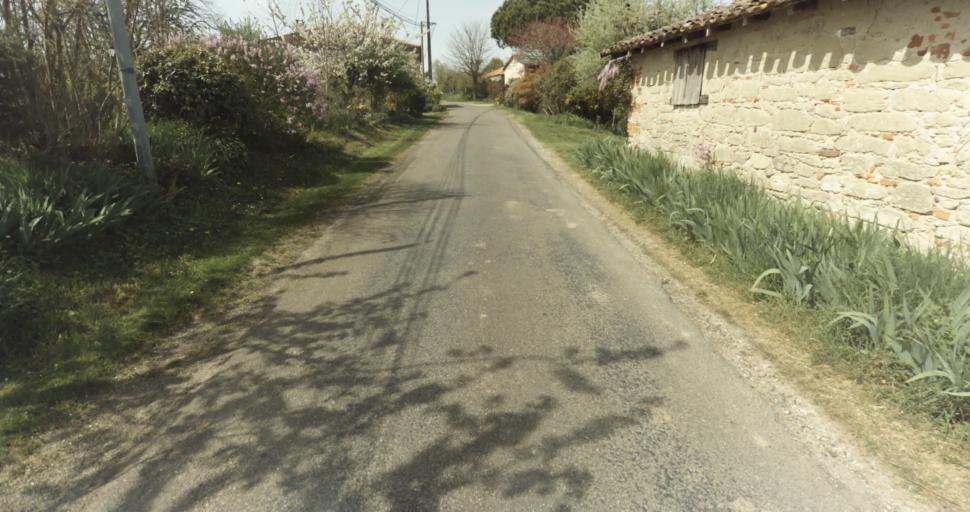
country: FR
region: Midi-Pyrenees
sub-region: Departement du Tarn-et-Garonne
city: Moissac
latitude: 44.1308
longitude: 1.0790
